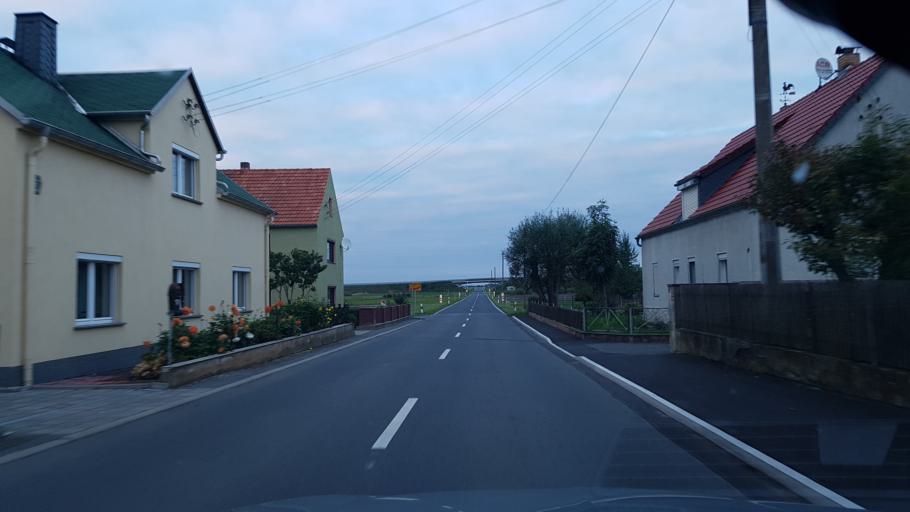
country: DE
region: Saxony
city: Grossenhain
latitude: 51.3012
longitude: 13.5898
